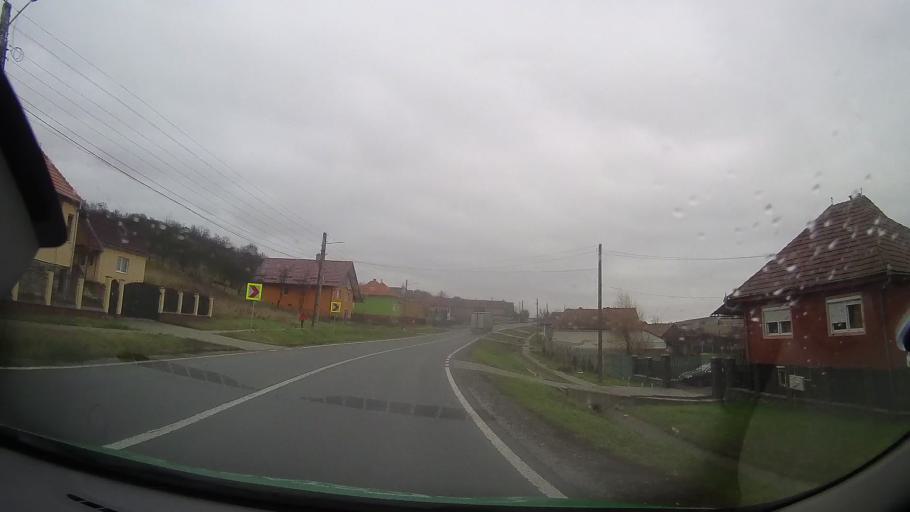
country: RO
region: Mures
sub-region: Comuna Lunca
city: Lunca
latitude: 46.8562
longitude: 24.5684
